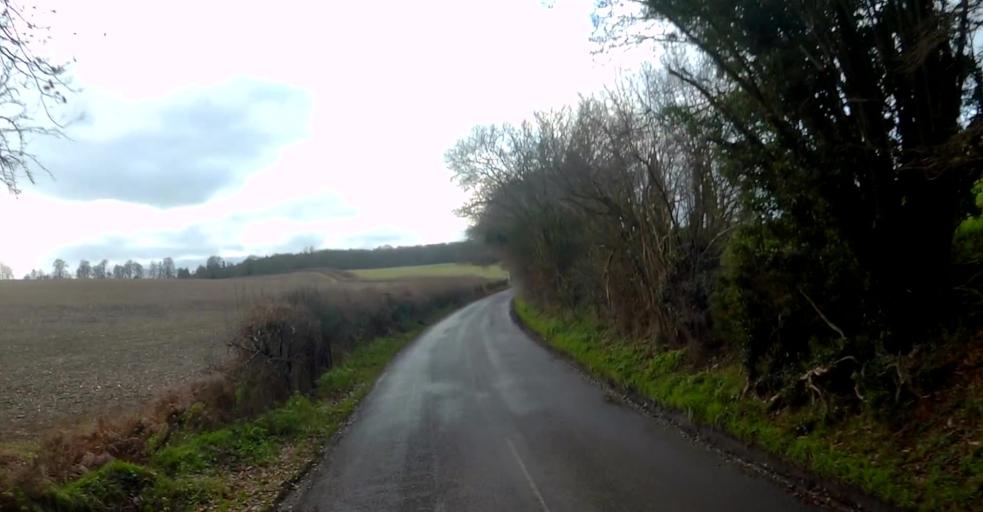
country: GB
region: England
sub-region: Hampshire
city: Basingstoke
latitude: 51.1913
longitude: -1.0734
